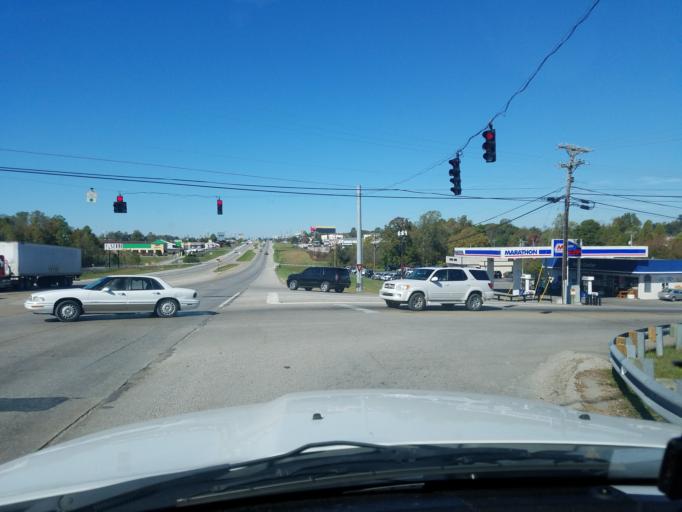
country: US
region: Kentucky
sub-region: Laurel County
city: North Corbin
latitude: 36.9716
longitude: -84.0920
